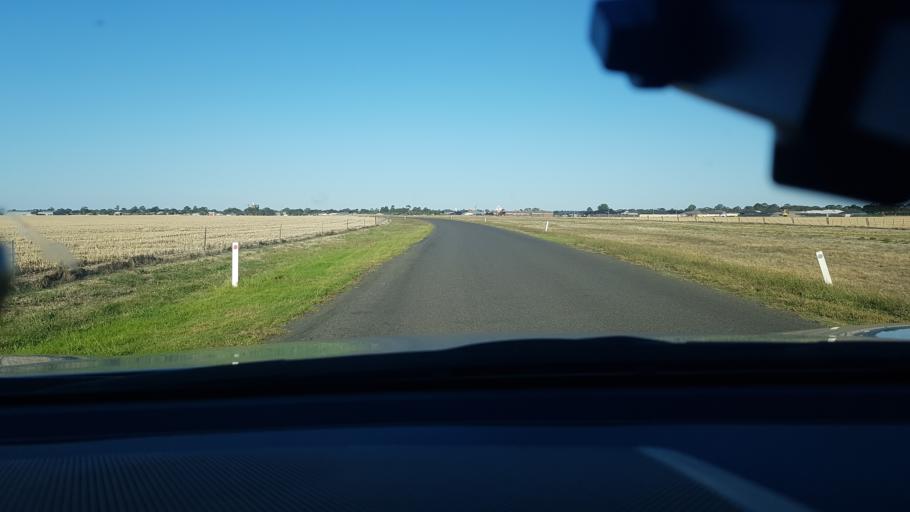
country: AU
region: Victoria
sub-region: Horsham
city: Horsham
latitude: -36.7134
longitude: 142.1691
